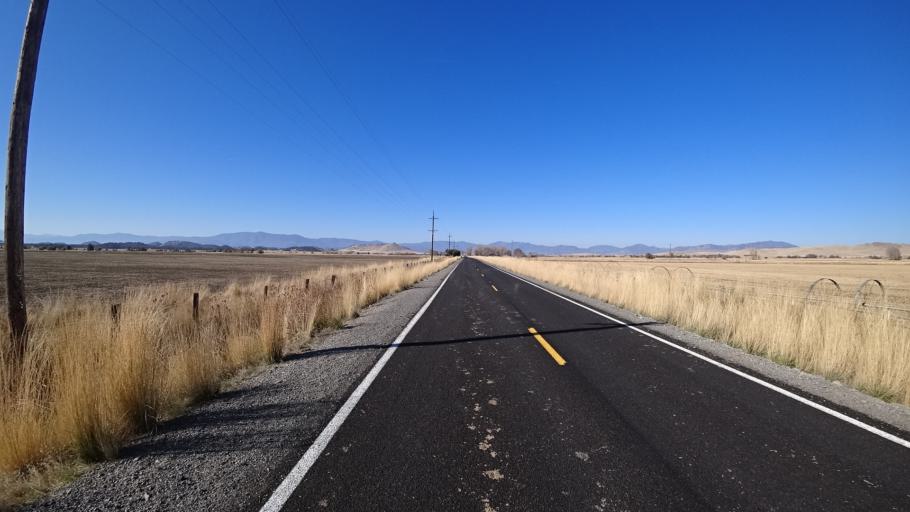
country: US
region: California
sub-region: Siskiyou County
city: Montague
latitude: 41.7115
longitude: -122.4015
